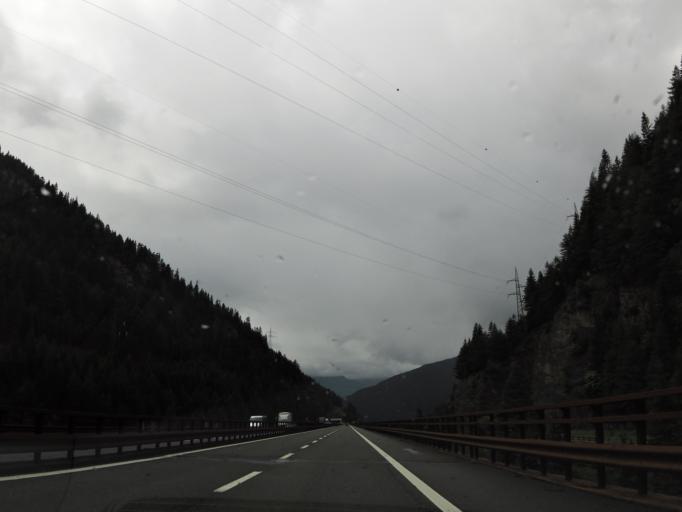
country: IT
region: Trentino-Alto Adige
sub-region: Bolzano
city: Colle Isarco
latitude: 46.9610
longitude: 11.4622
